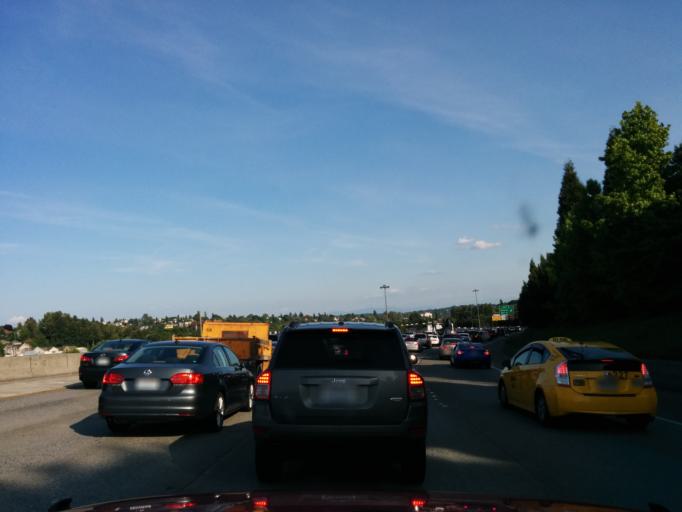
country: US
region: Washington
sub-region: King County
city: Seattle
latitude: 47.5942
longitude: -122.3134
